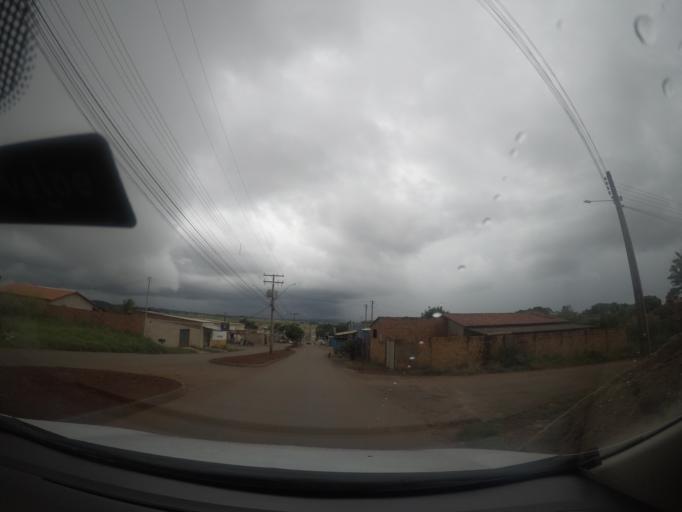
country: BR
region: Goias
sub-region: Trindade
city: Trindade
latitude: -16.6128
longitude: -49.3924
